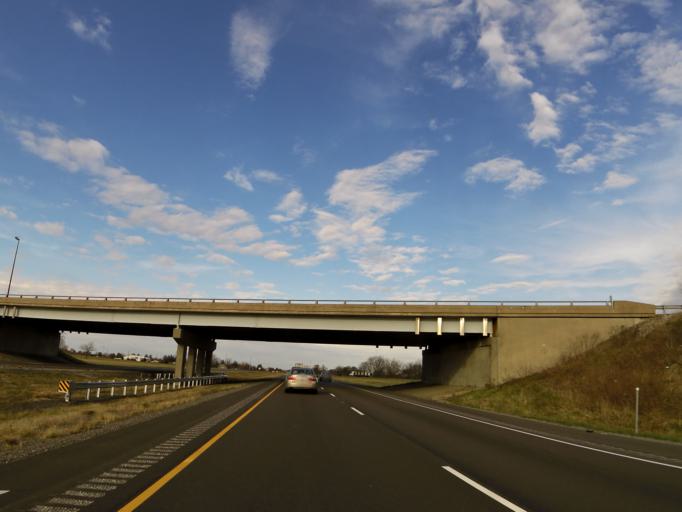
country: US
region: Illinois
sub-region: Washington County
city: Okawville
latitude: 38.4395
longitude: -89.5295
